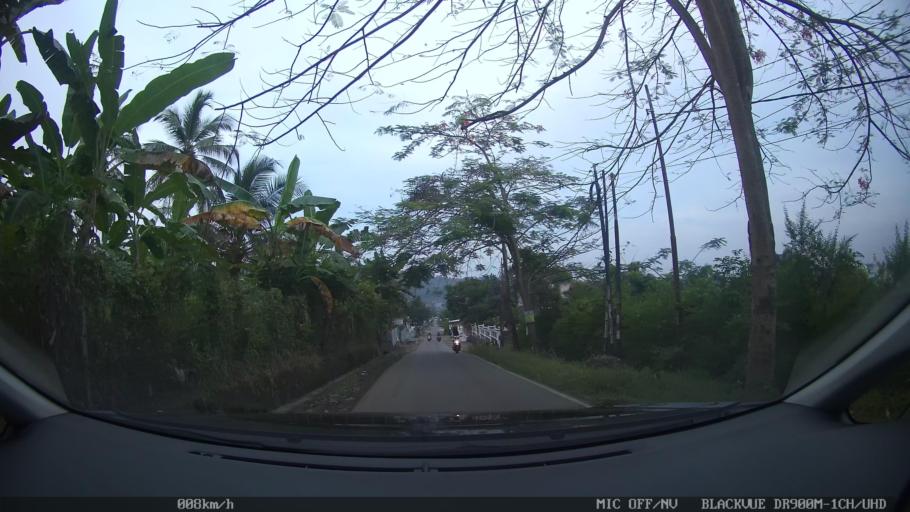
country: ID
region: Lampung
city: Kedaton
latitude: -5.4021
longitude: 105.2339
